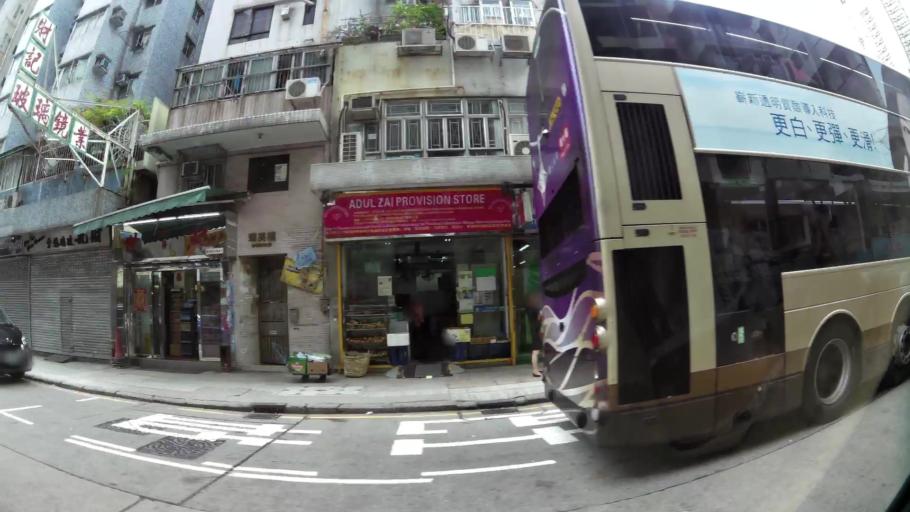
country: HK
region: Sham Shui Po
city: Sham Shui Po
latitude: 22.3271
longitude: 114.1604
